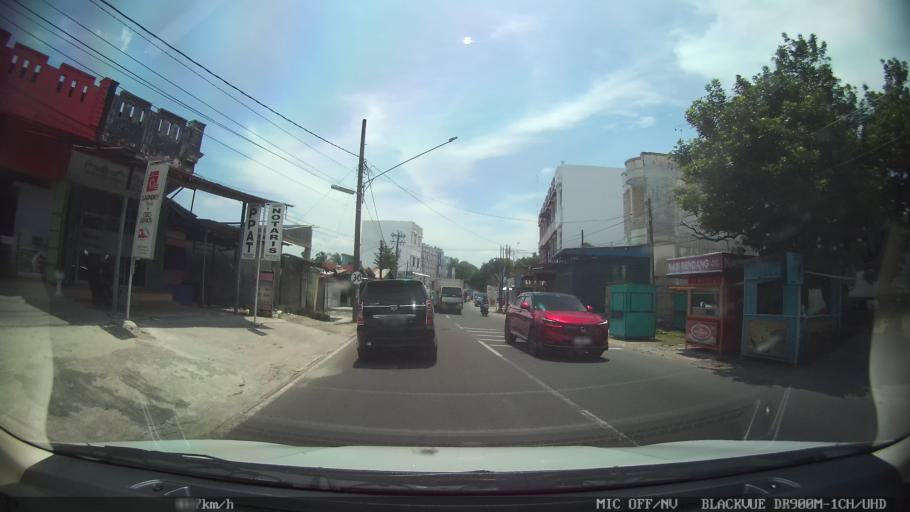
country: ID
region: North Sumatra
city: Binjai
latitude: 3.6002
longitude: 98.4863
